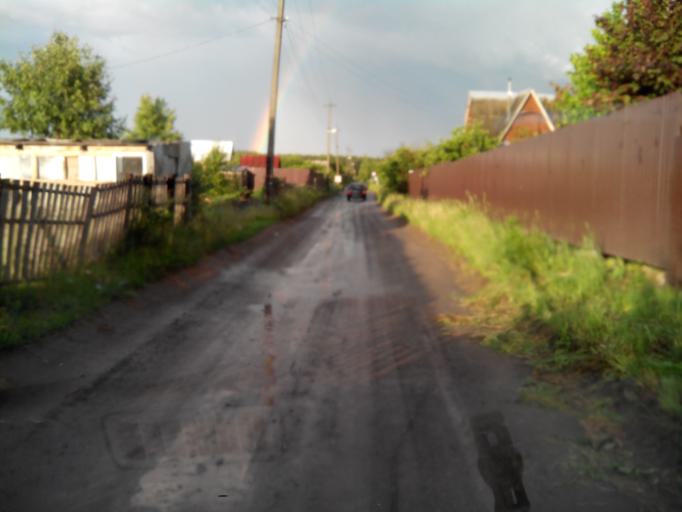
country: RU
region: Penza
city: Zasechnoye
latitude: 53.0388
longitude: 45.0464
